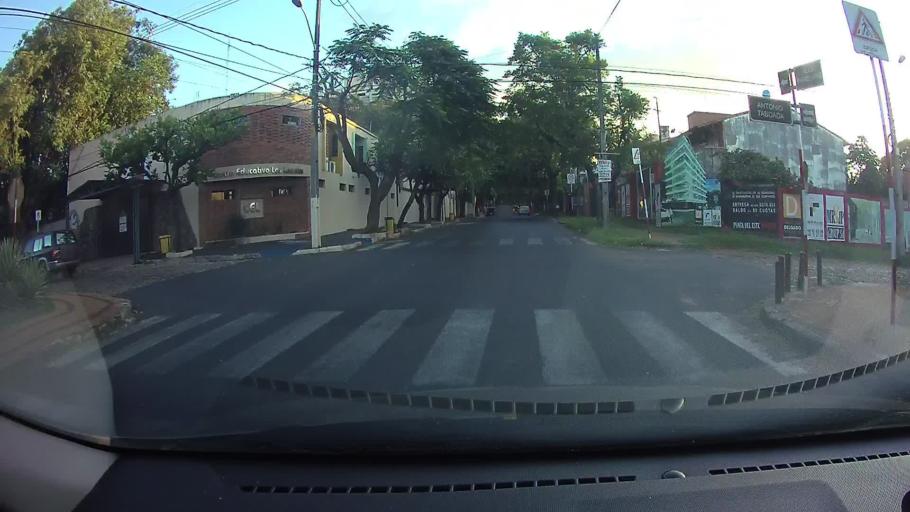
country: PY
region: Central
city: Lambare
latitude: -25.3070
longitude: -57.5775
